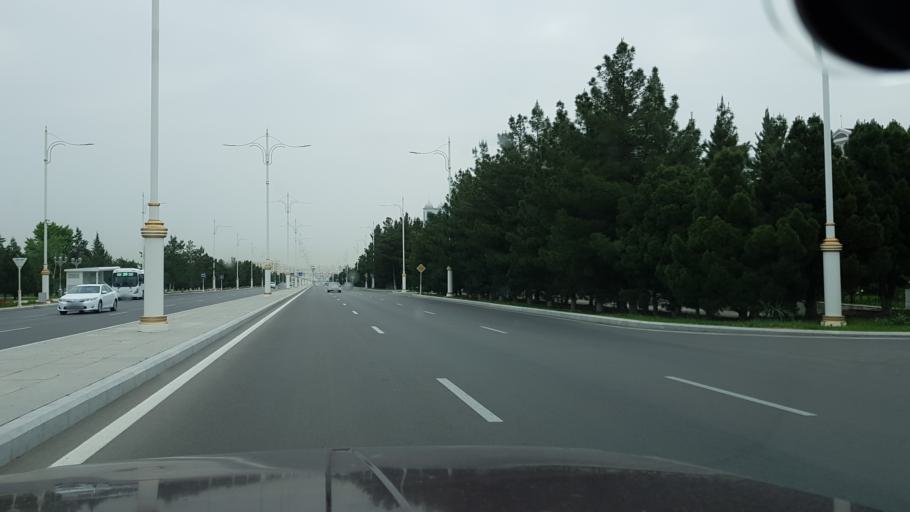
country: TM
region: Ahal
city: Ashgabat
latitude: 37.8870
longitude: 58.3878
